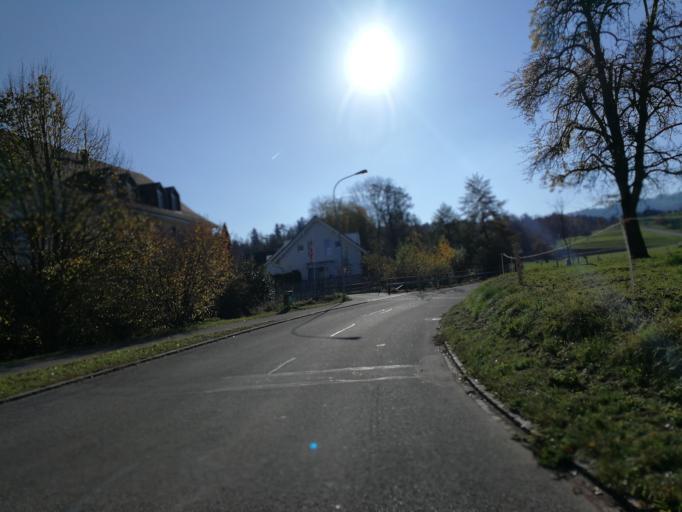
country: CH
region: Zurich
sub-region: Bezirk Uster
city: Monchaltorf
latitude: 47.3088
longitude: 8.7162
